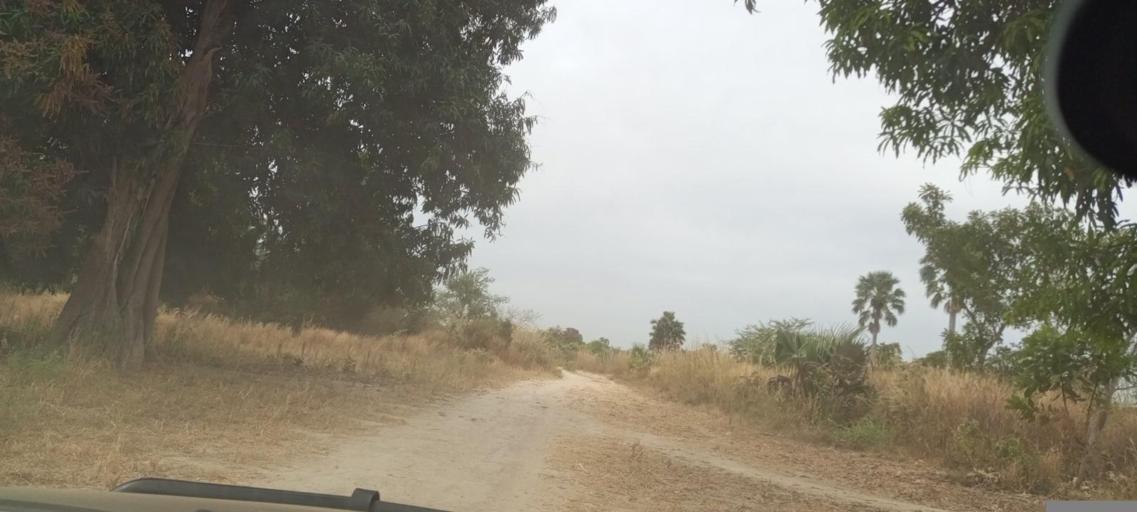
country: ML
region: Koulikoro
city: Kati
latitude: 12.7566
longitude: -8.3063
